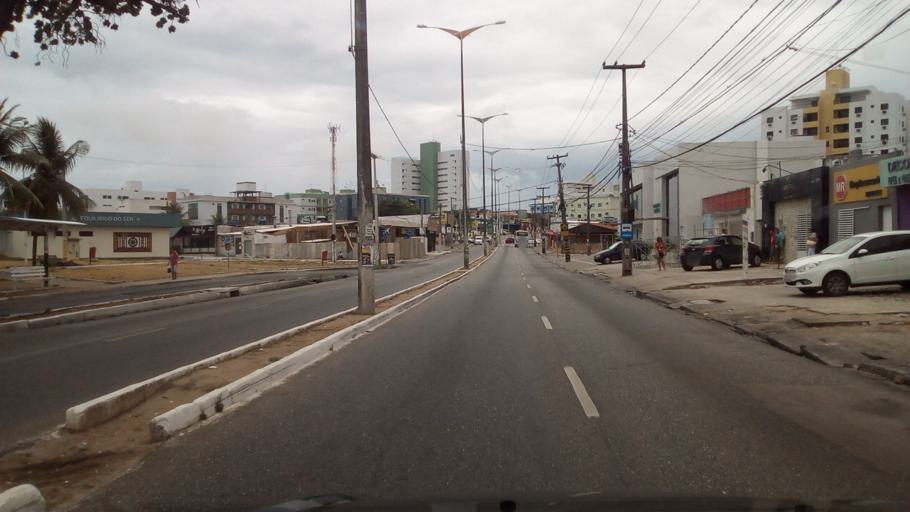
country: BR
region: Paraiba
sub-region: Joao Pessoa
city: Joao Pessoa
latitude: -7.1500
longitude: -34.8411
